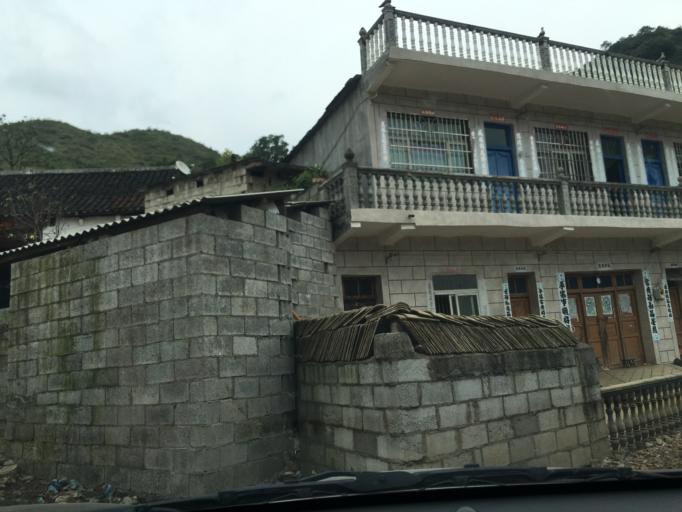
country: CN
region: Guangxi Zhuangzu Zizhiqu
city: Xinzhou
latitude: 25.3745
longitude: 105.6317
